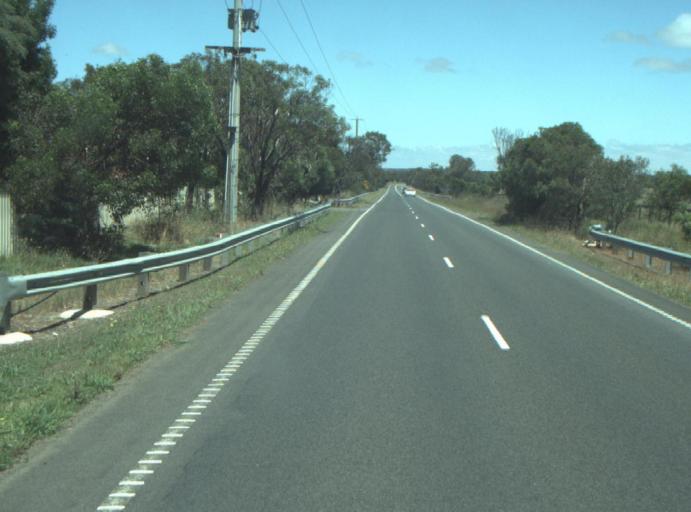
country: AU
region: Victoria
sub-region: Queenscliffe
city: Queenscliff
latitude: -38.1831
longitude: 144.6878
